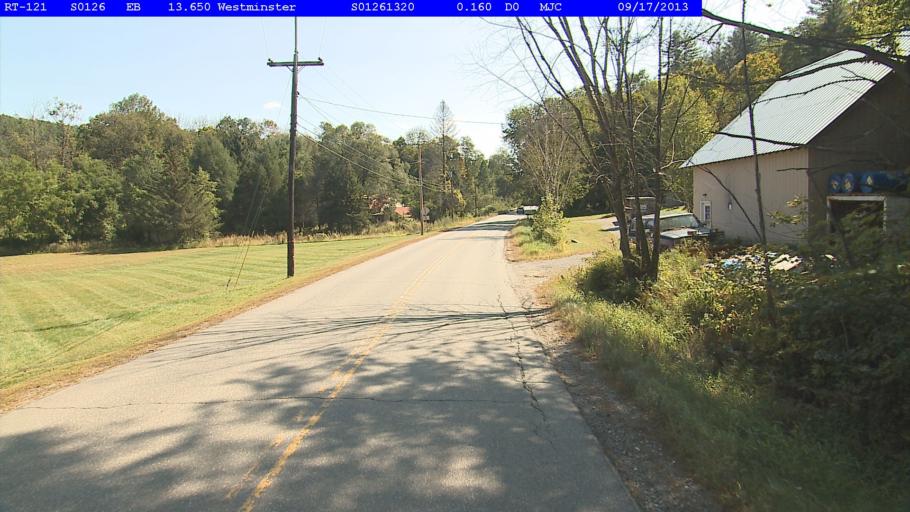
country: US
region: Vermont
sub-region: Windham County
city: Bellows Falls
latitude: 43.1249
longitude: -72.4744
